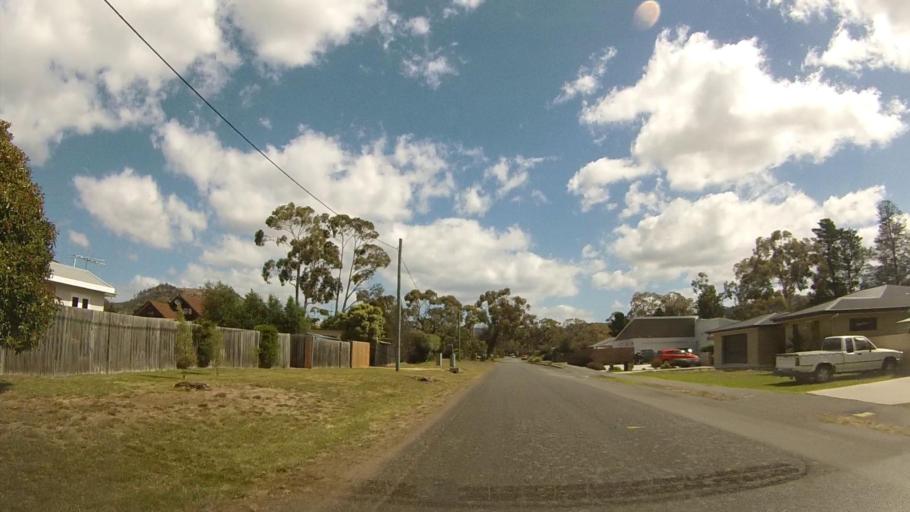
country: AU
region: Tasmania
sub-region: Clarence
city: Seven Mile Beach
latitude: -42.8557
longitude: 147.5048
